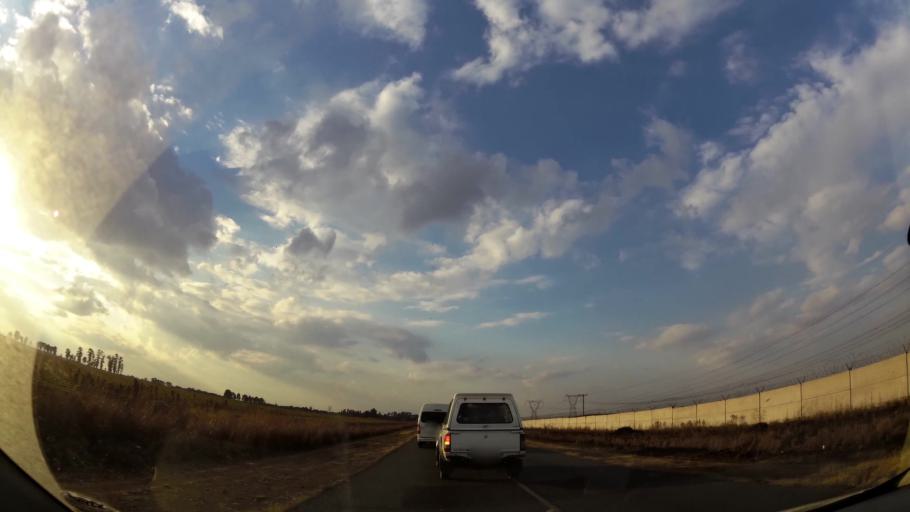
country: ZA
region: Gauteng
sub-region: Sedibeng District Municipality
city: Vanderbijlpark
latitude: -26.6521
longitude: 27.8029
